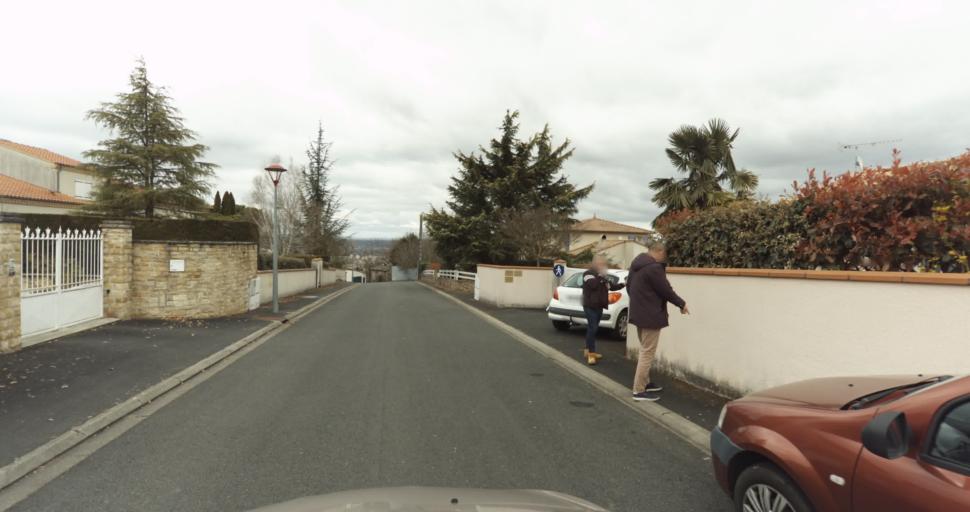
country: FR
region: Midi-Pyrenees
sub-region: Departement du Tarn
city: Puygouzon
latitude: 43.9053
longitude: 2.1639
